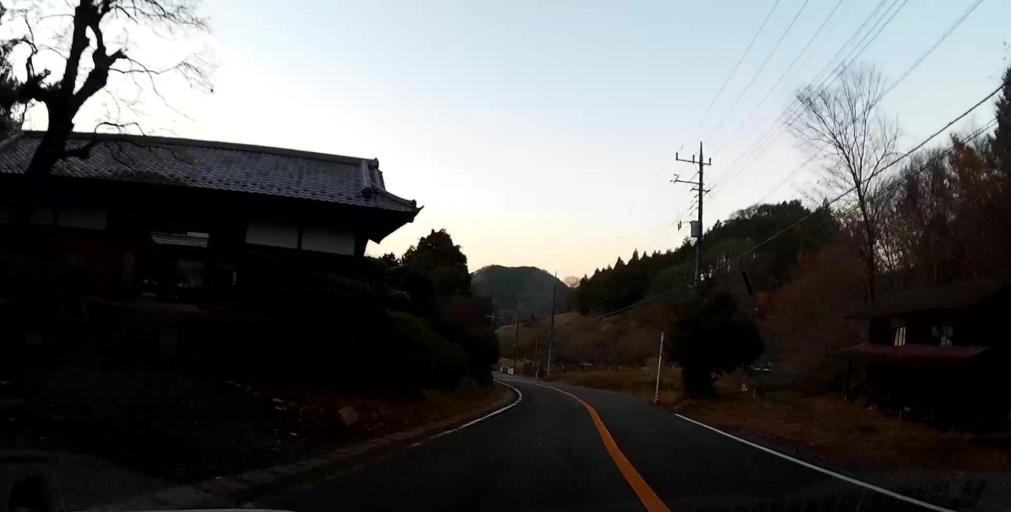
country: JP
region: Yamanashi
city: Uenohara
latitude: 35.5843
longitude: 139.1749
